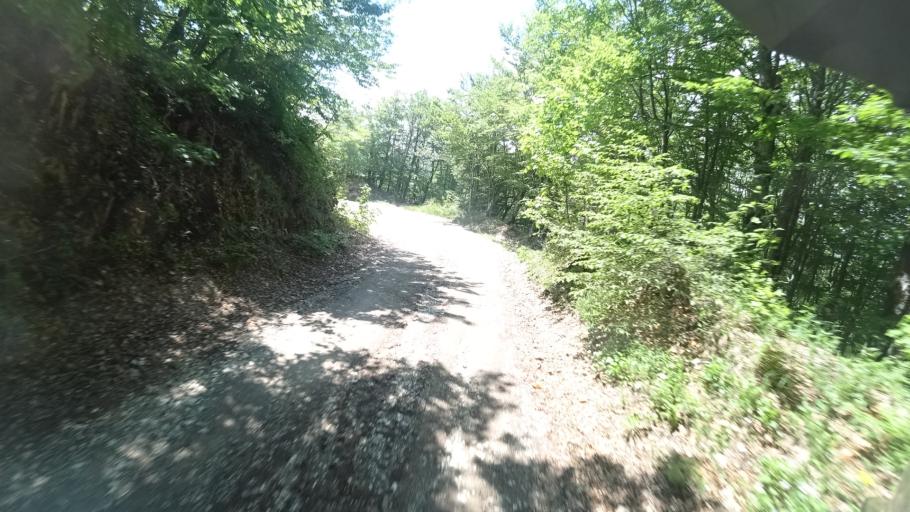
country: BA
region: Federation of Bosnia and Herzegovina
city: Orasac
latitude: 44.5759
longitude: 15.8520
